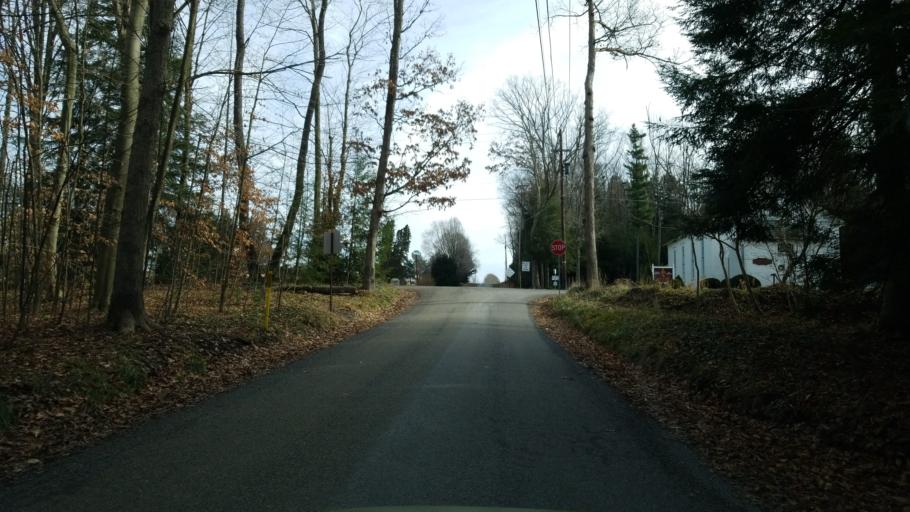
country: US
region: Pennsylvania
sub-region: Indiana County
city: Johnsonburg
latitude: 40.9395
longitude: -78.8845
